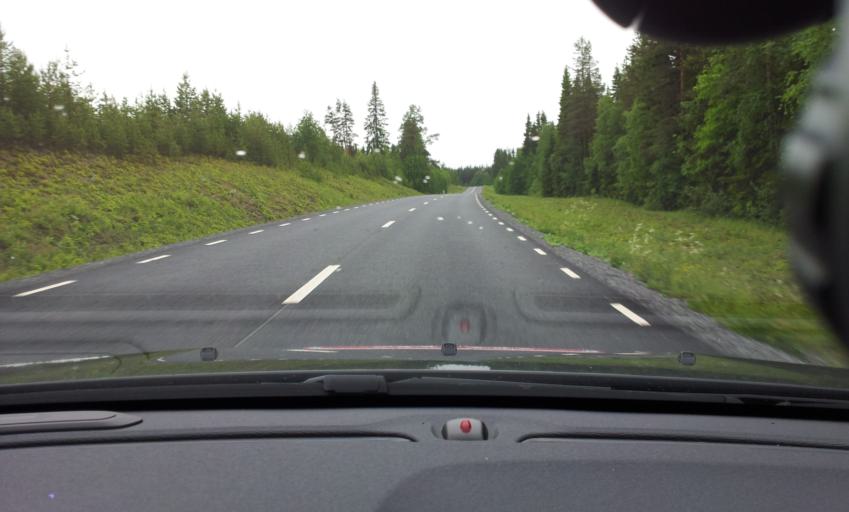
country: SE
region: Jaemtland
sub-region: Stroemsunds Kommun
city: Stroemsund
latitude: 63.6615
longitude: 15.1472
